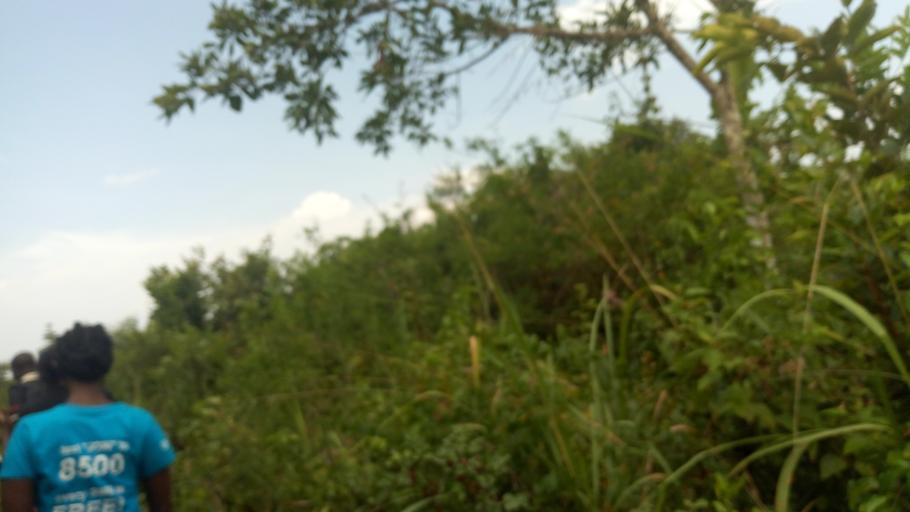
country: UG
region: Western Region
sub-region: Kiryandongo District
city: Kiryandongo
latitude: 1.8414
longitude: 32.0195
